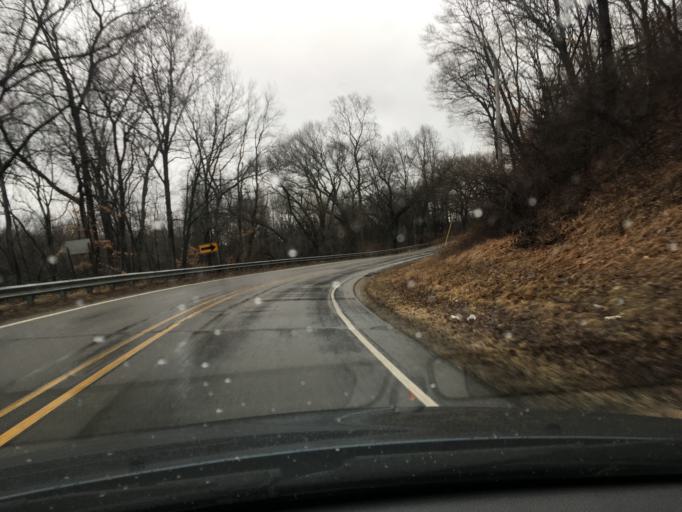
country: US
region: Michigan
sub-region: Jackson County
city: Grass Lake
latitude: 42.3152
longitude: -84.1552
